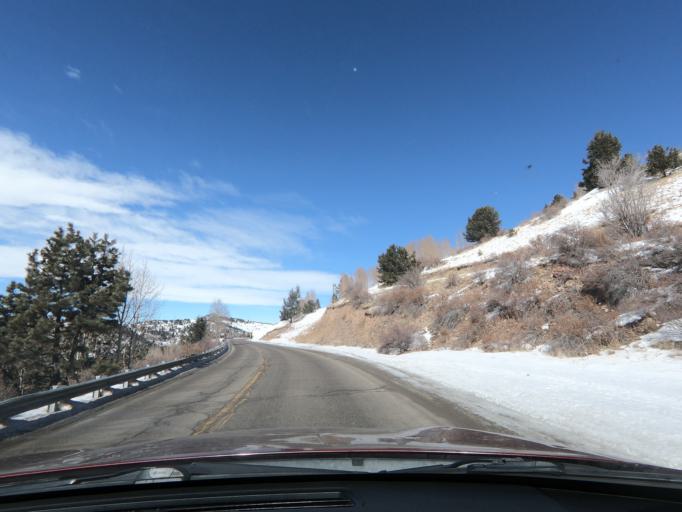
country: US
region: Colorado
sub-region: Teller County
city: Cripple Creek
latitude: 38.7230
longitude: -105.1656
